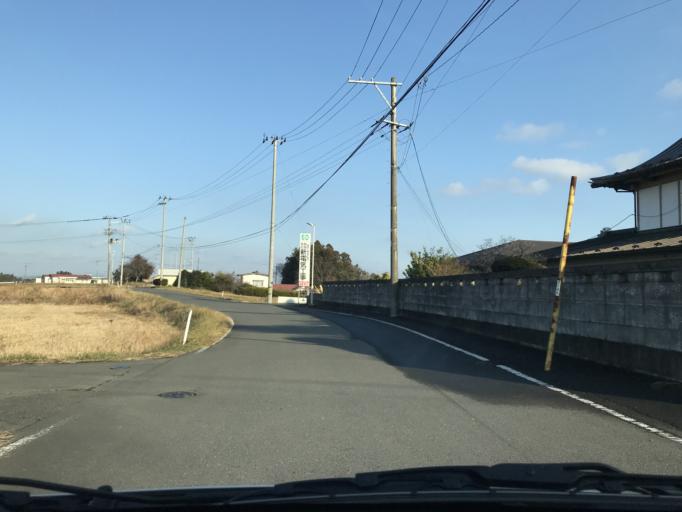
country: JP
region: Miyagi
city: Wakuya
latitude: 38.6956
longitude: 141.1207
